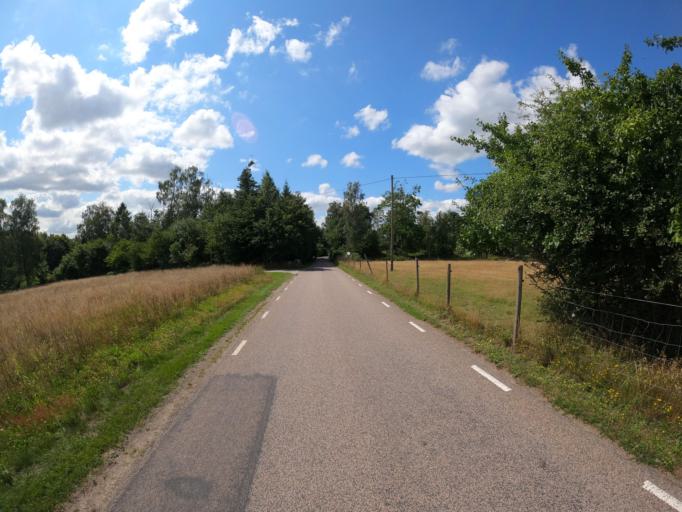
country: SE
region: Skane
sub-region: Lunds Kommun
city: Veberod
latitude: 55.5852
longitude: 13.4850
